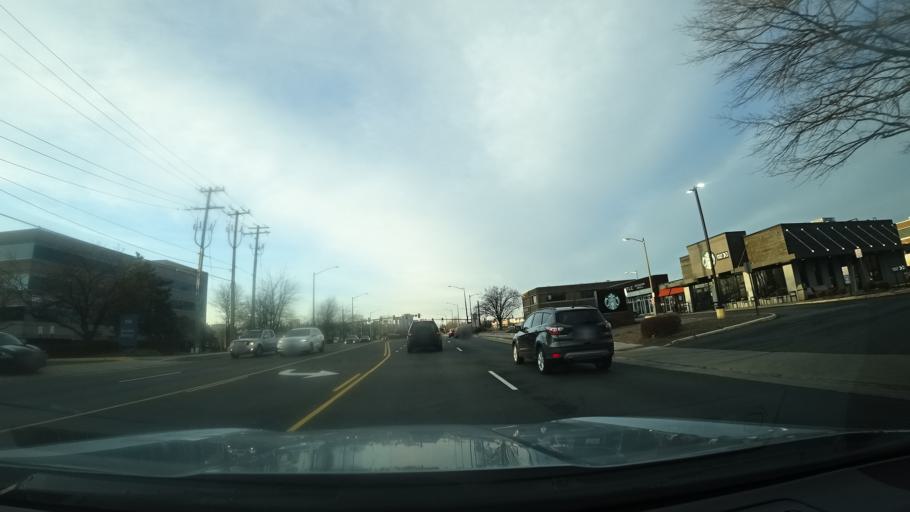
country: US
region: Virginia
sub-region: Fairfax County
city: Herndon
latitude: 38.9640
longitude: -77.3984
